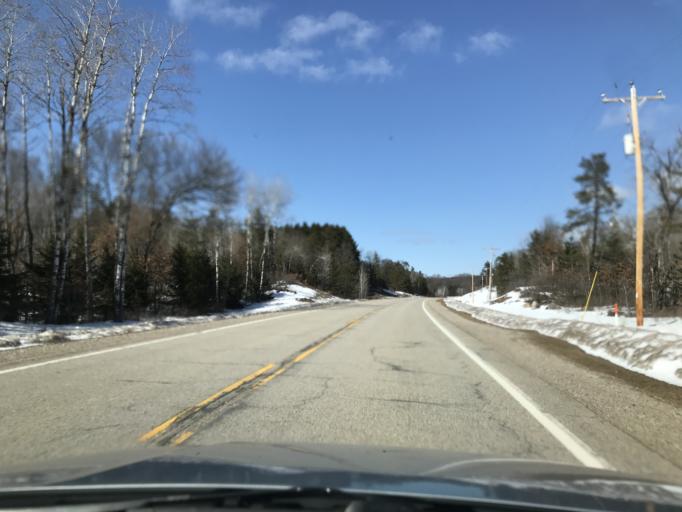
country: US
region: Wisconsin
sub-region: Marinette County
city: Peshtigo
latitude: 45.3318
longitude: -88.1019
